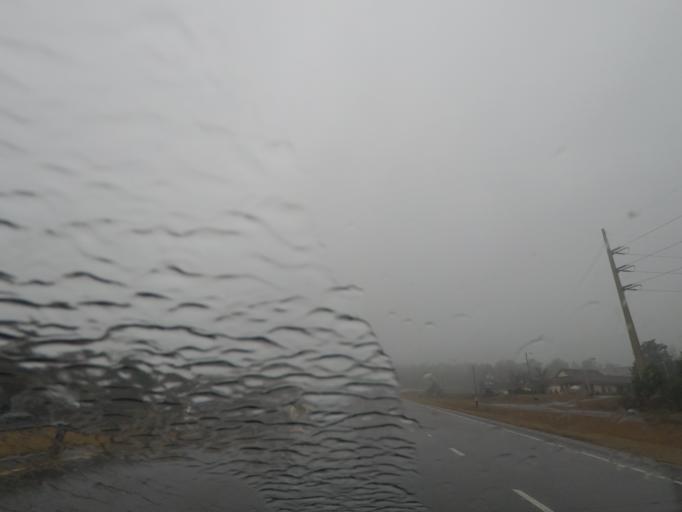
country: US
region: North Carolina
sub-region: Moore County
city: Southern Pines
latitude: 35.1733
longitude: -79.4043
